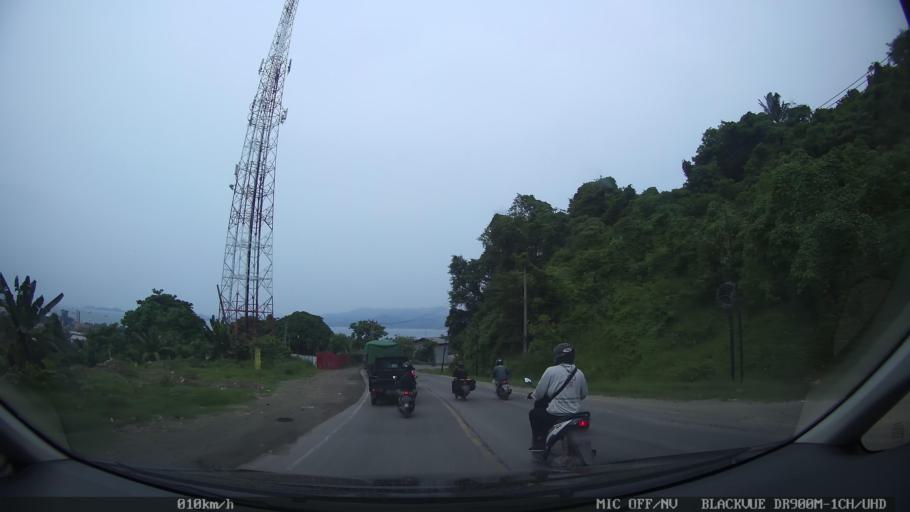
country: ID
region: Lampung
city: Panjang
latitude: -5.4414
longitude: 105.3130
